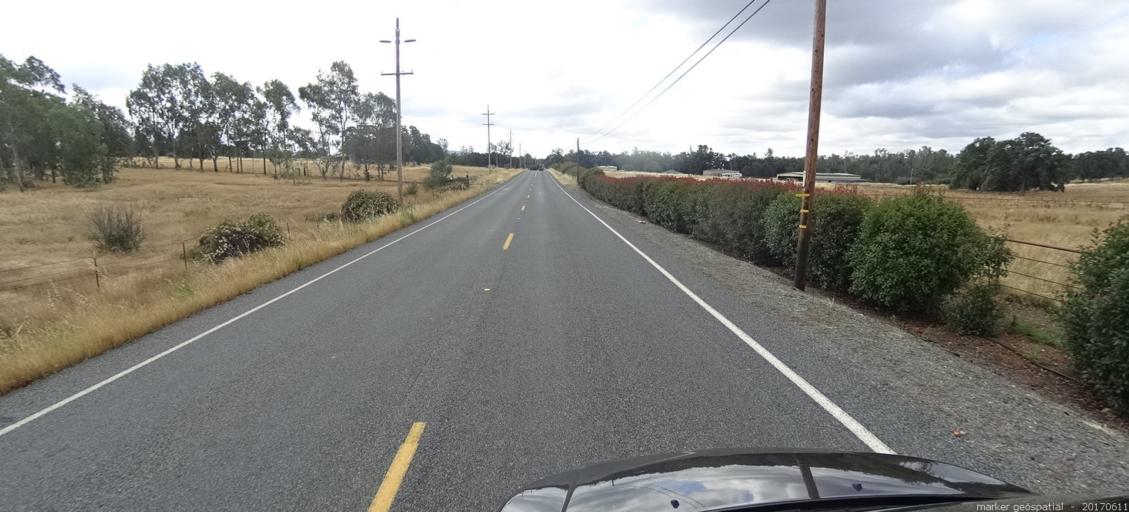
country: US
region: California
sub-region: Yuba County
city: Loma Rica
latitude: 39.3958
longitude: -121.4130
